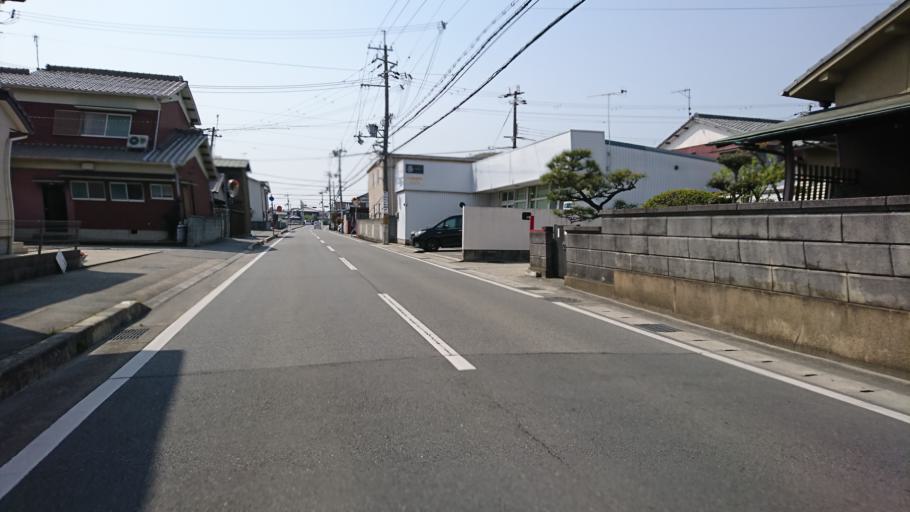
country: JP
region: Hyogo
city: Shirahamacho-usazakiminami
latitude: 34.7869
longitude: 134.7510
